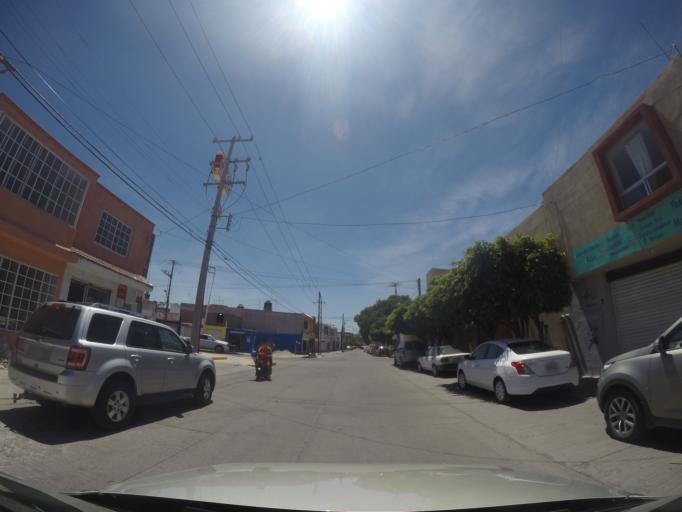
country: MX
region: San Luis Potosi
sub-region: San Luis Potosi
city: San Luis Potosi
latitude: 22.1586
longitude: -100.9920
